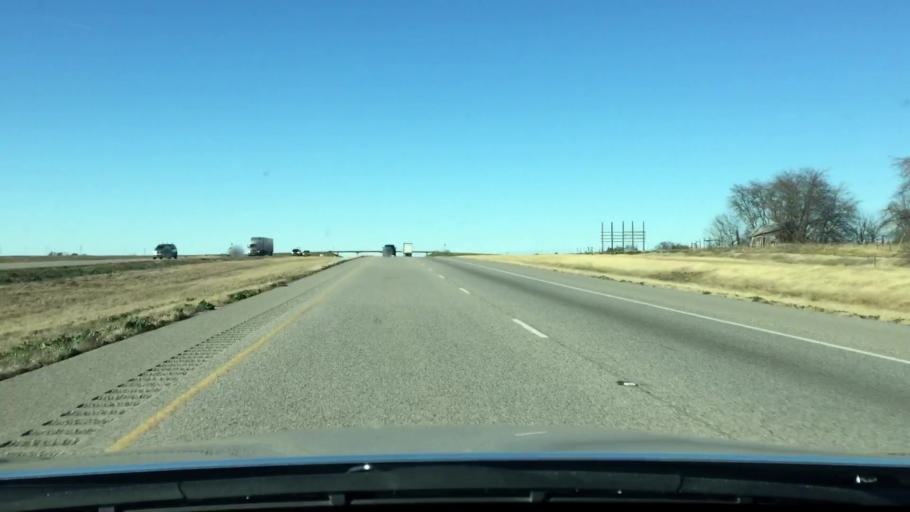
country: US
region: Texas
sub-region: Hill County
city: Itasca
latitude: 32.1190
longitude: -97.1157
